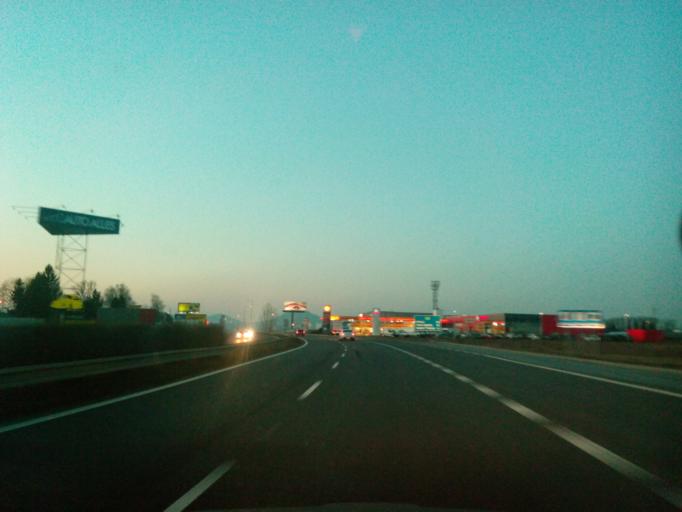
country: SK
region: Presovsky
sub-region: Okres Presov
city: Presov
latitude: 48.9540
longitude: 21.2577
